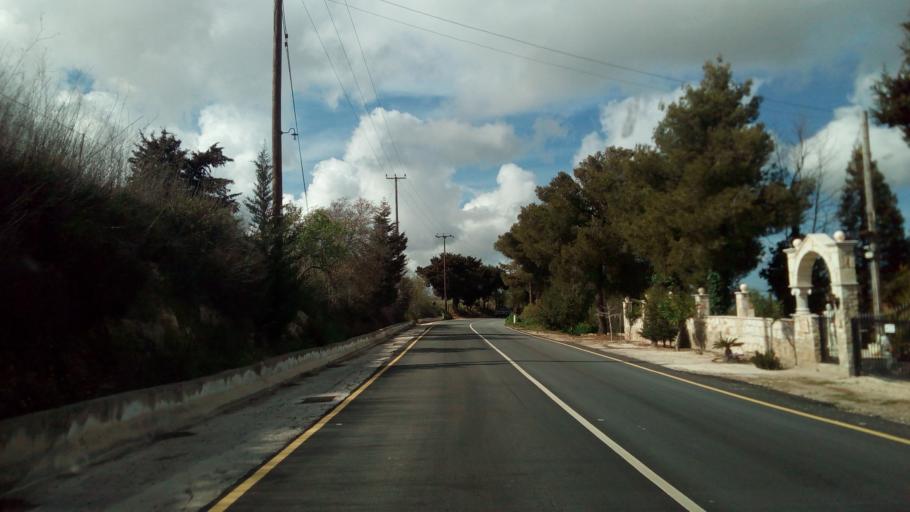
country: CY
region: Pafos
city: Pegeia
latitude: 34.9181
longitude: 32.4230
